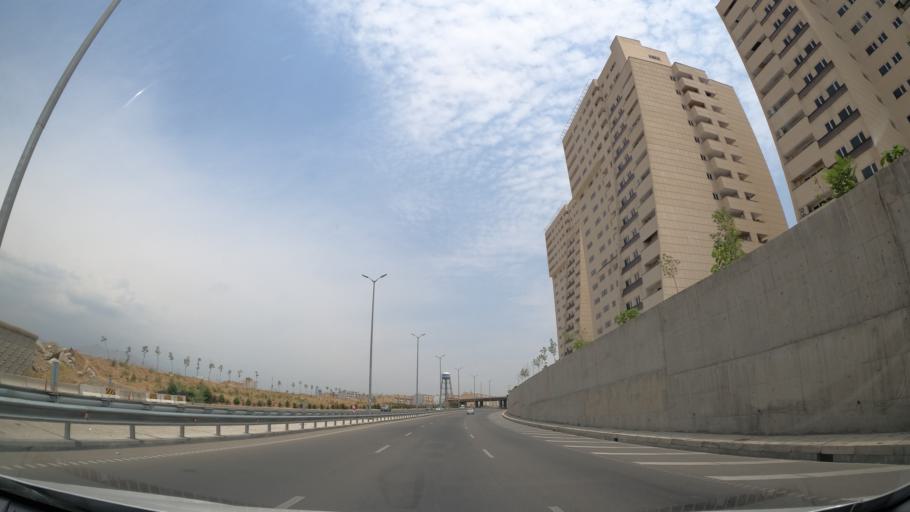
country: IR
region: Tehran
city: Shahr-e Qods
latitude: 35.7413
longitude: 51.2428
